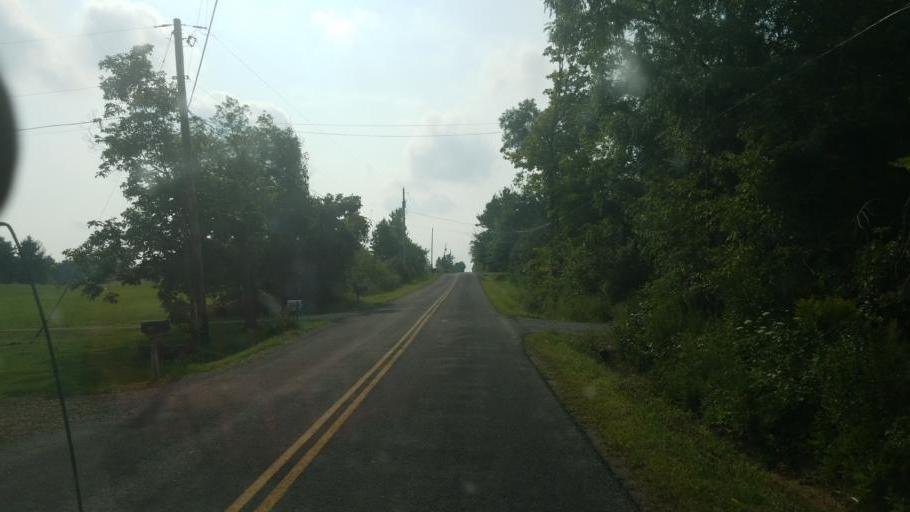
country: US
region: Ohio
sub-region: Medina County
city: Westfield Center
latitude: 41.0518
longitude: -81.9344
